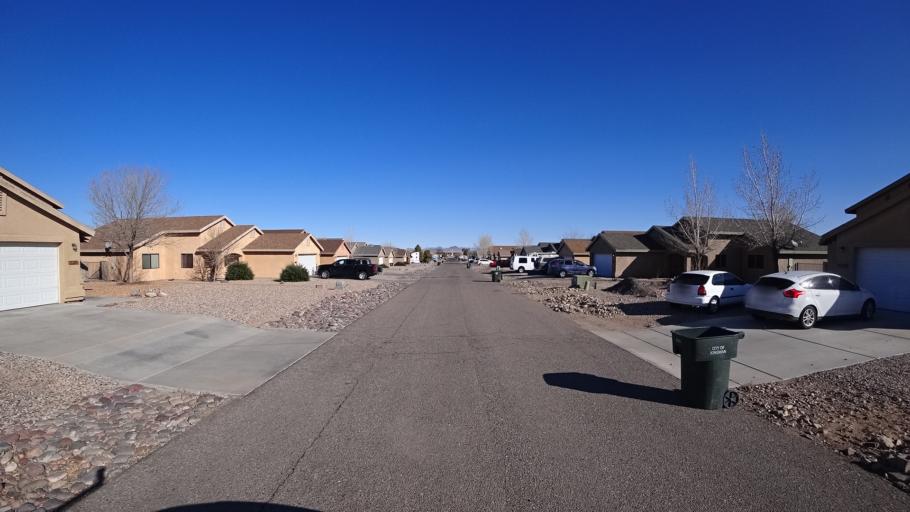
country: US
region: Arizona
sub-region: Mohave County
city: Kingman
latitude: 35.2106
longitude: -114.0068
